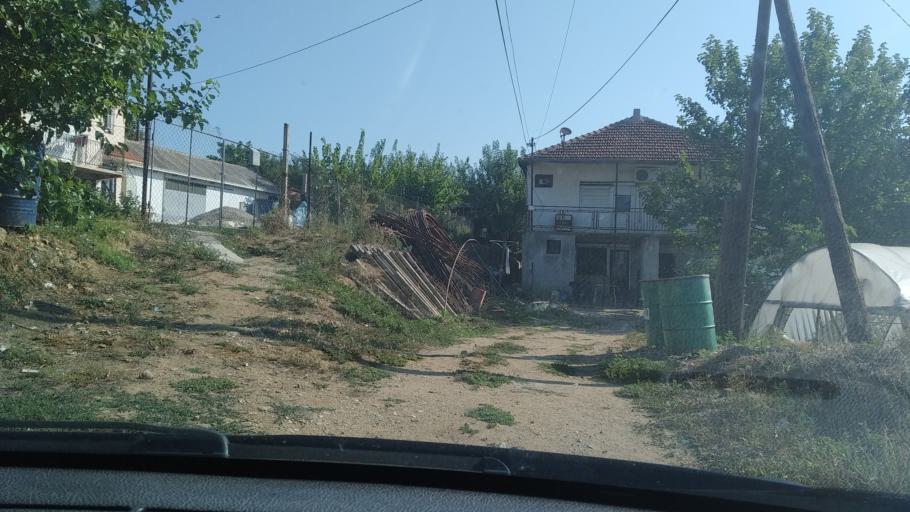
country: MK
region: Bogdanci
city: Bogdanci
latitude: 41.2067
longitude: 22.5826
